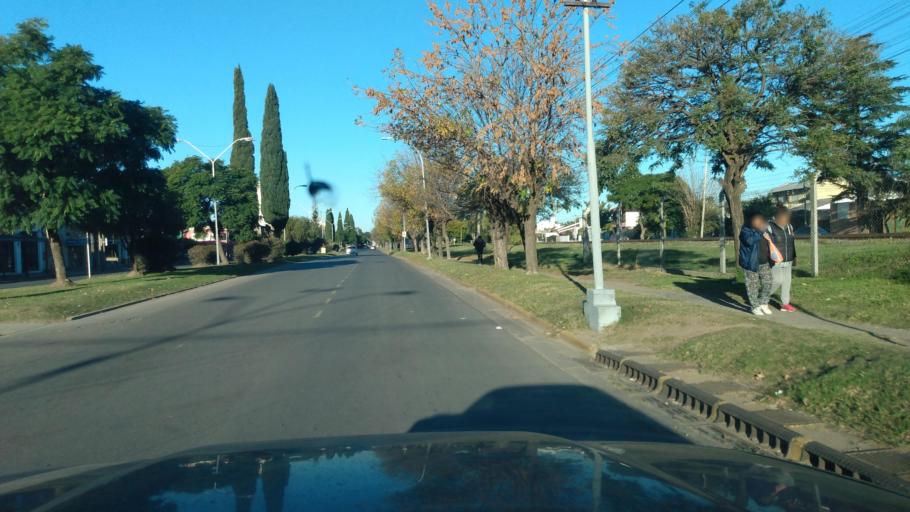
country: AR
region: Buenos Aires
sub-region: Partido de General Rodriguez
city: General Rodriguez
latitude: -34.6097
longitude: -58.9485
